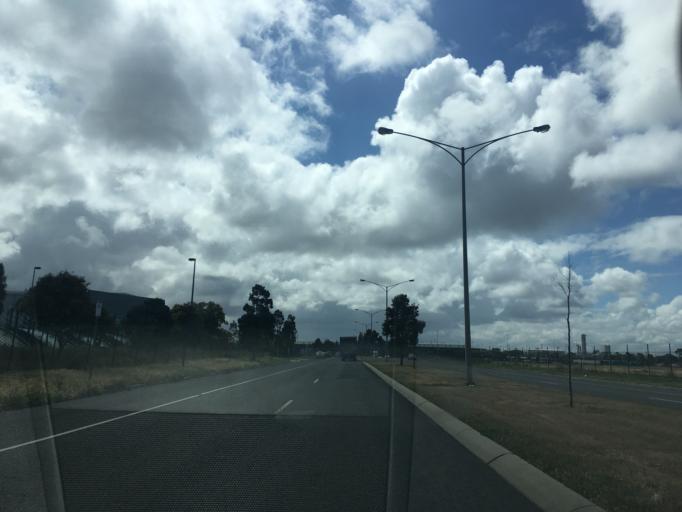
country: AU
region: Victoria
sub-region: Hobsons Bay
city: Altona
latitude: -37.8441
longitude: 144.8099
